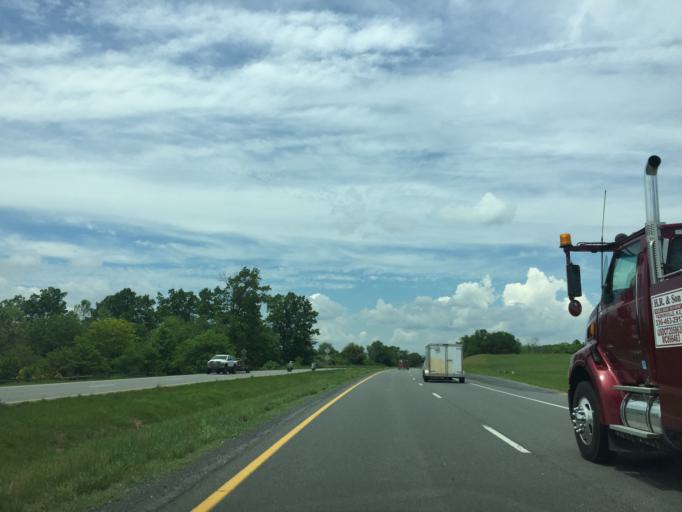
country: US
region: Virginia
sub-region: Frederick County
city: Shawnee Land
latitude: 39.2747
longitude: -78.2524
